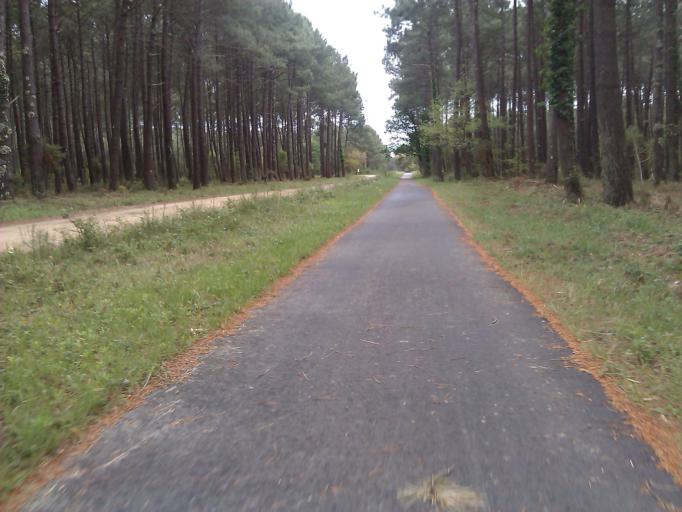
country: FR
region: Aquitaine
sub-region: Departement des Landes
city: Vielle-Saint-Girons
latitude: 43.9315
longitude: -1.3525
